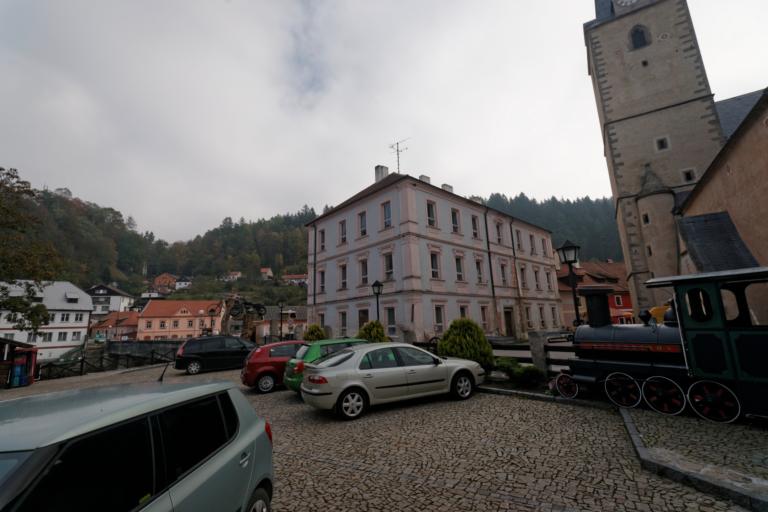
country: CZ
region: Jihocesky
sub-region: Okres Cesky Krumlov
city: Vyssi Brod
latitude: 48.6552
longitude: 14.3670
